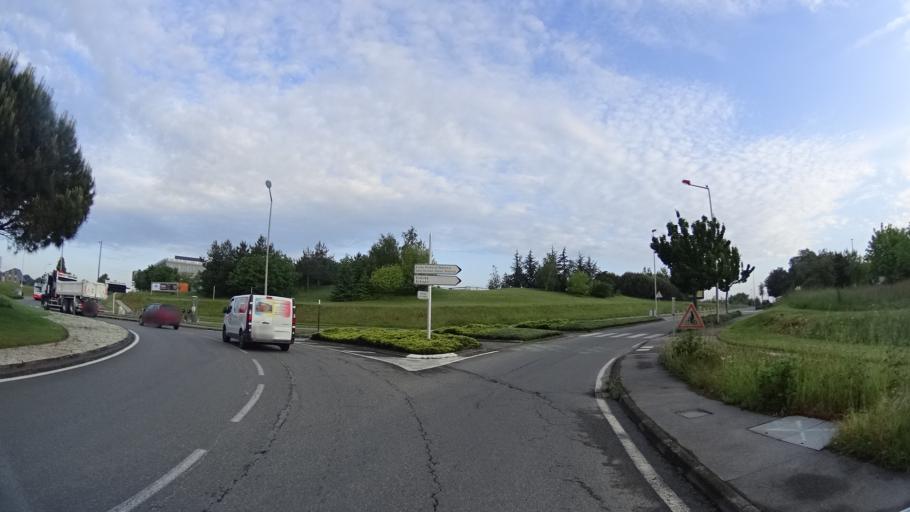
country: FR
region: Brittany
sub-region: Departement du Morbihan
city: Vannes
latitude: 47.6443
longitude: -2.7436
